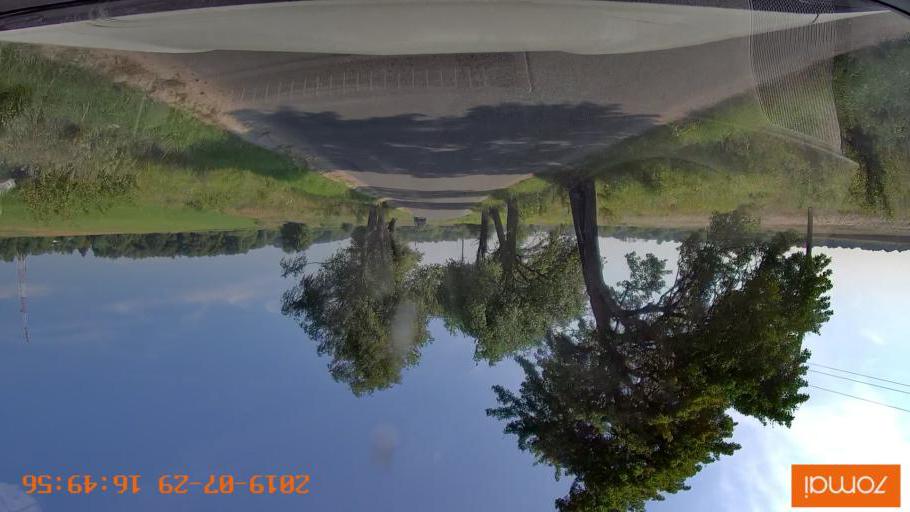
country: RU
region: Kaliningrad
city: Primorsk
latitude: 54.7987
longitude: 20.0597
